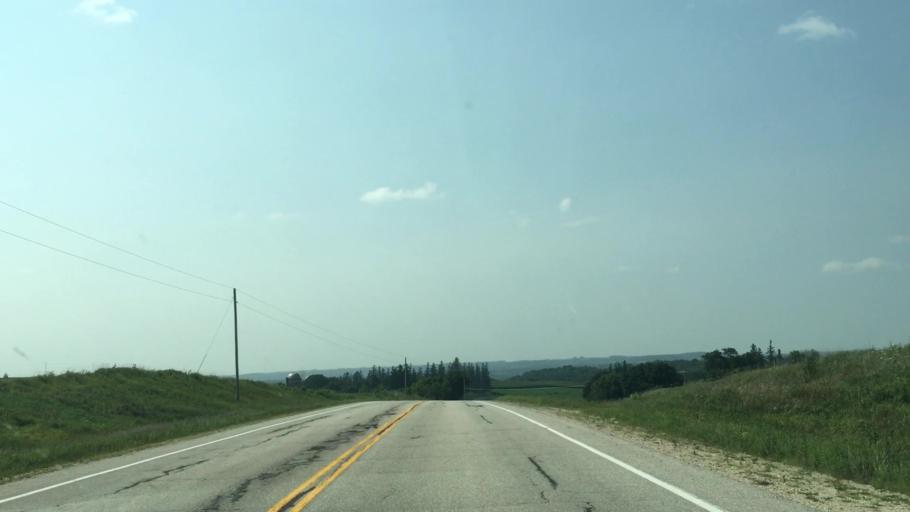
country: US
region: Minnesota
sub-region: Fillmore County
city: Preston
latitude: 43.6896
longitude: -91.9451
